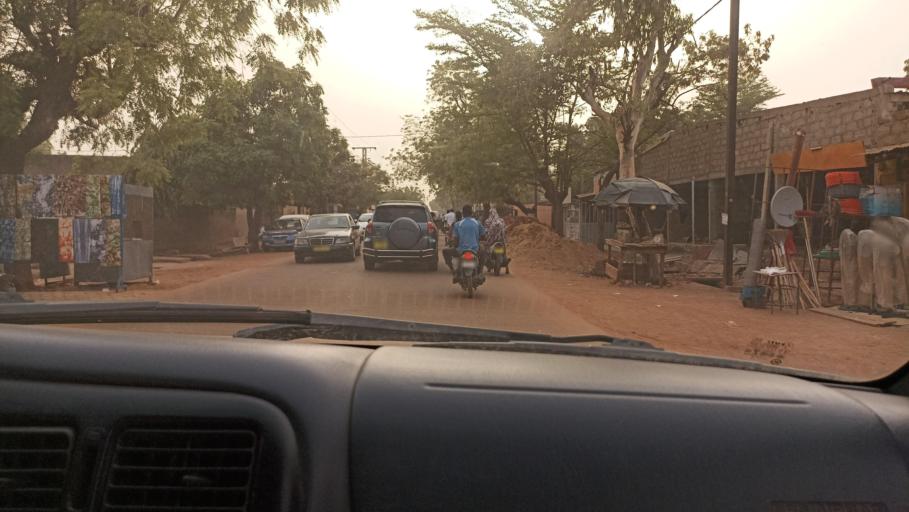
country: BF
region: Centre
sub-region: Kadiogo Province
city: Ouagadougou
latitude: 12.3805
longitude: -1.5438
